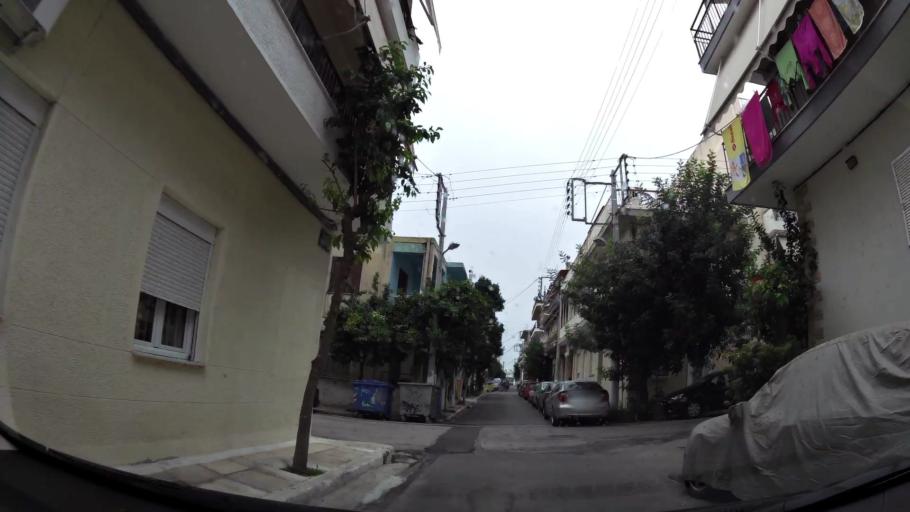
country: GR
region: Attica
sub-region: Nomarchia Athinas
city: Chaidari
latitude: 37.9993
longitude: 23.6695
